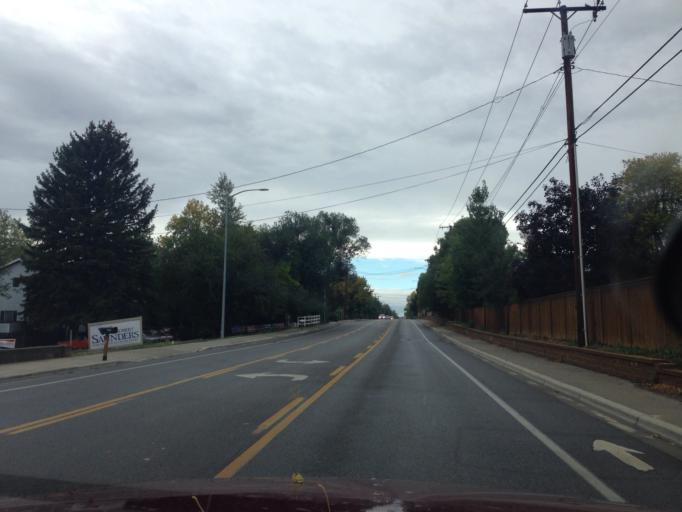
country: US
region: Montana
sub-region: Yellowstone County
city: Billings
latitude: 45.7987
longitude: -108.5701
